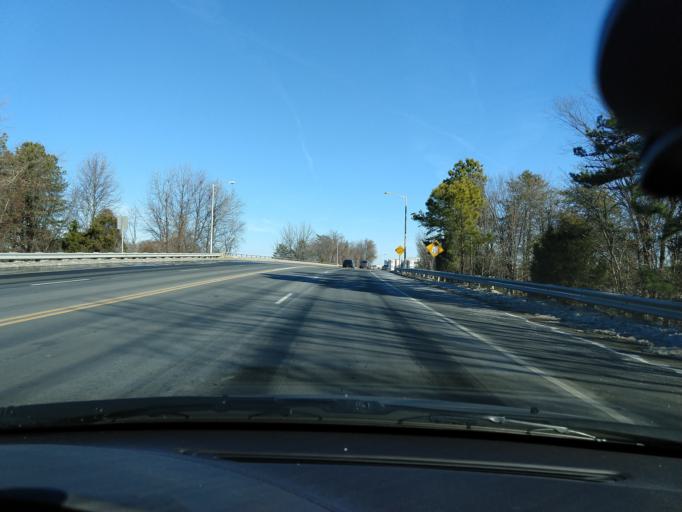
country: US
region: North Carolina
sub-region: Guilford County
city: Greensboro
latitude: 36.0647
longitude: -79.7993
